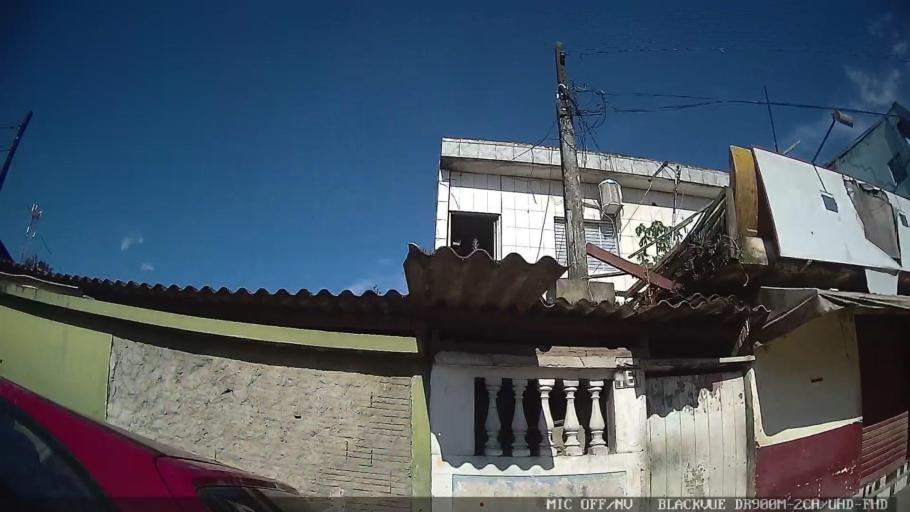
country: BR
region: Sao Paulo
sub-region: Santos
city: Santos
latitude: -23.9531
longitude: -46.2978
